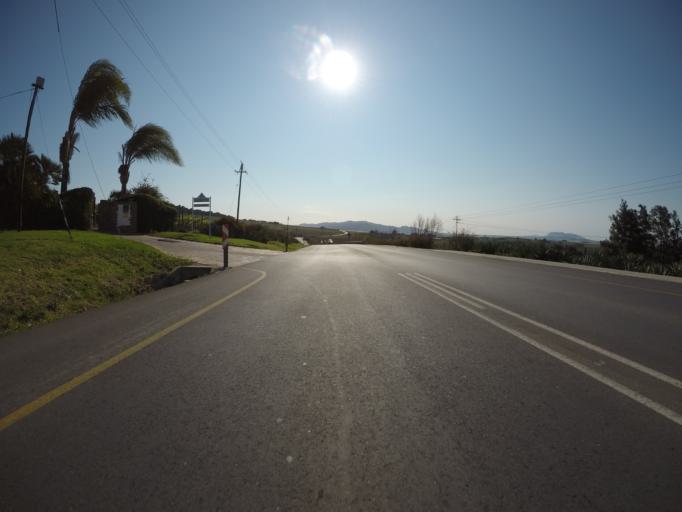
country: ZA
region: Western Cape
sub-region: Cape Winelands District Municipality
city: Noorder-Paarl
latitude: -33.6784
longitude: 18.9440
